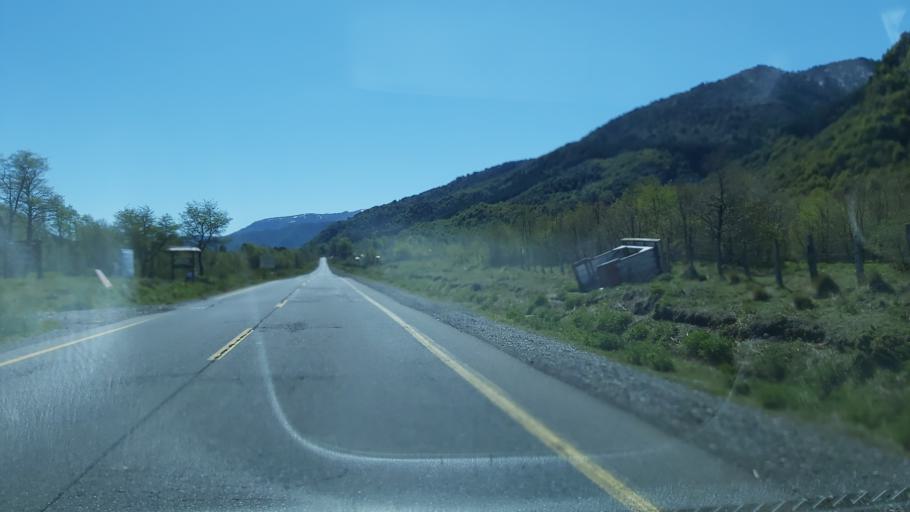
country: CL
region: Araucania
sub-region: Provincia de Cautin
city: Vilcun
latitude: -38.4750
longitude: -71.5507
